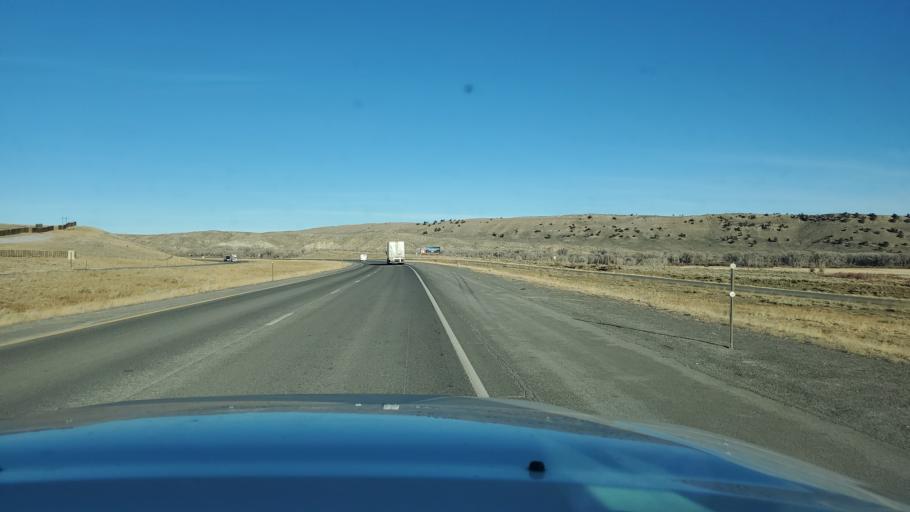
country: US
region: Wyoming
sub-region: Carbon County
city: Saratoga
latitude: 41.6935
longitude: -106.3838
